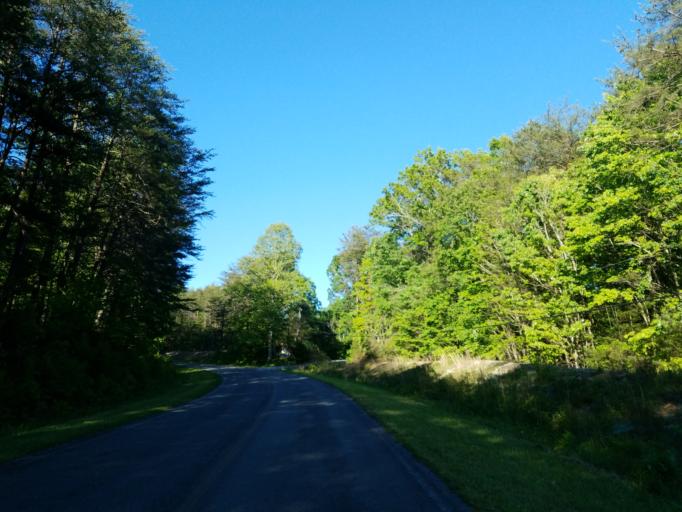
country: US
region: Georgia
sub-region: Fannin County
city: Blue Ridge
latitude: 34.7112
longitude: -84.2928
